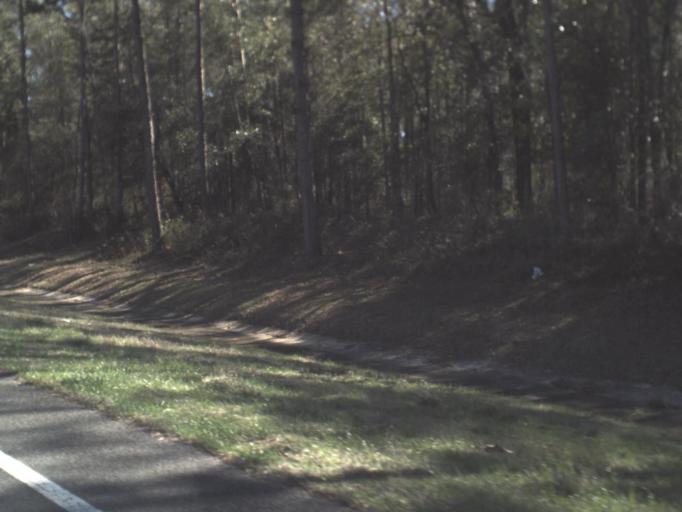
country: US
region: Florida
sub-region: Gadsden County
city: Midway
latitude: 30.5435
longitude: -84.4824
